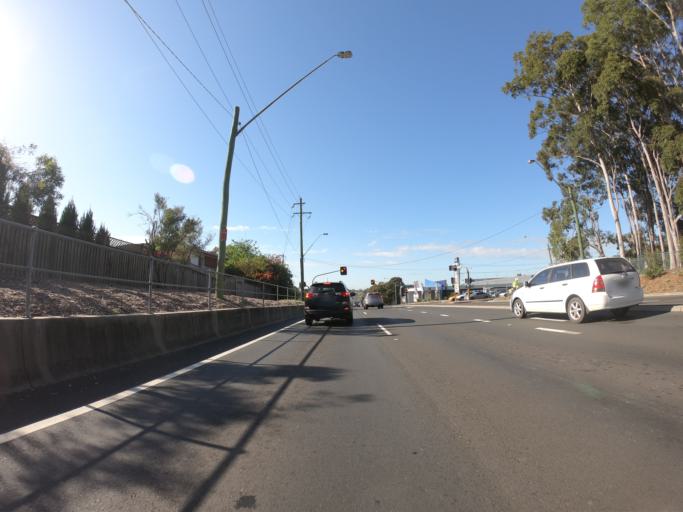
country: AU
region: New South Wales
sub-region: The Hills Shire
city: Castle Hill
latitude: -33.7244
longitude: 150.9767
